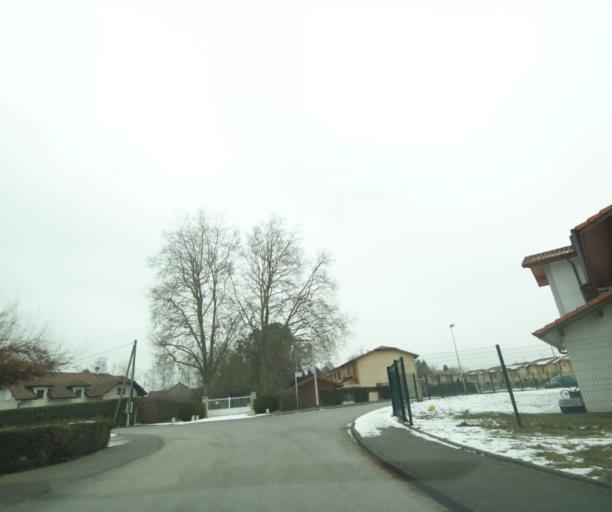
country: FR
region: Rhone-Alpes
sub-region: Departement de la Haute-Savoie
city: Reignier-Esery
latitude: 46.1404
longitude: 6.2744
